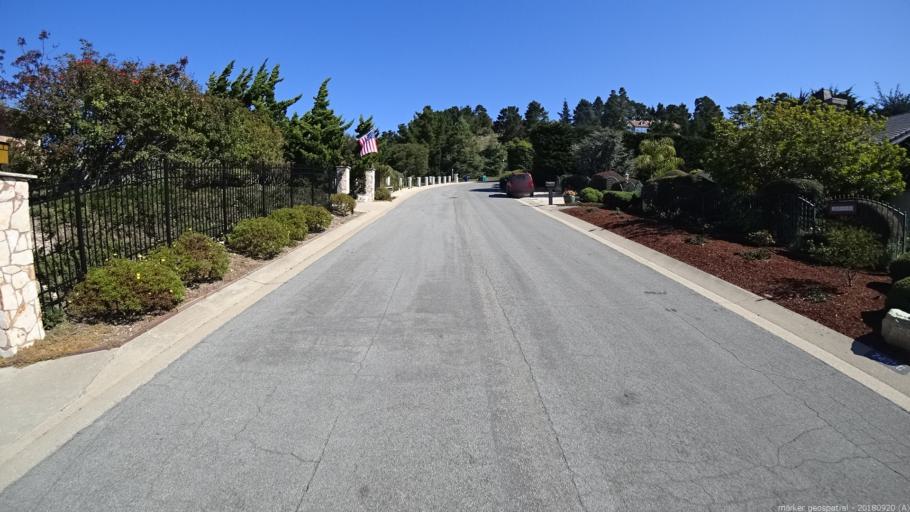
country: US
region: California
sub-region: Monterey County
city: Carmel-by-the-Sea
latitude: 36.5630
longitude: -121.9001
